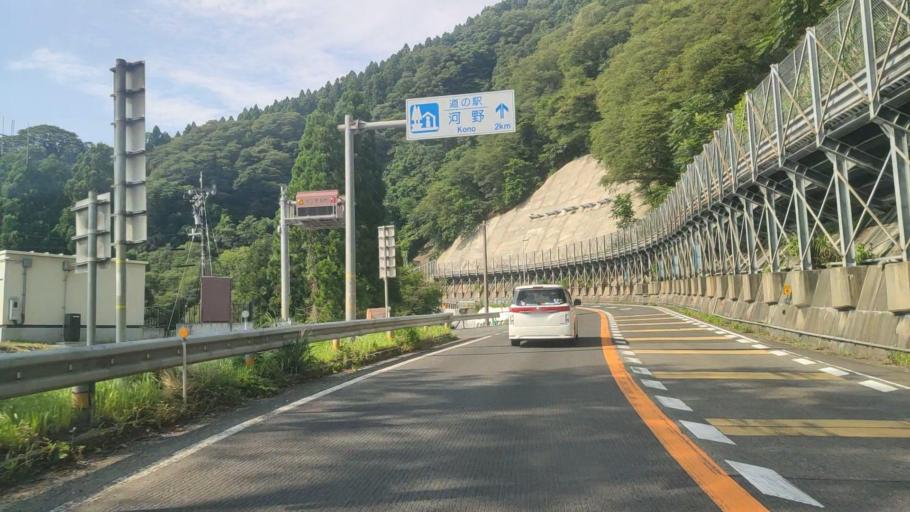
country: JP
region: Fukui
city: Takefu
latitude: 35.7816
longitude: 136.1013
